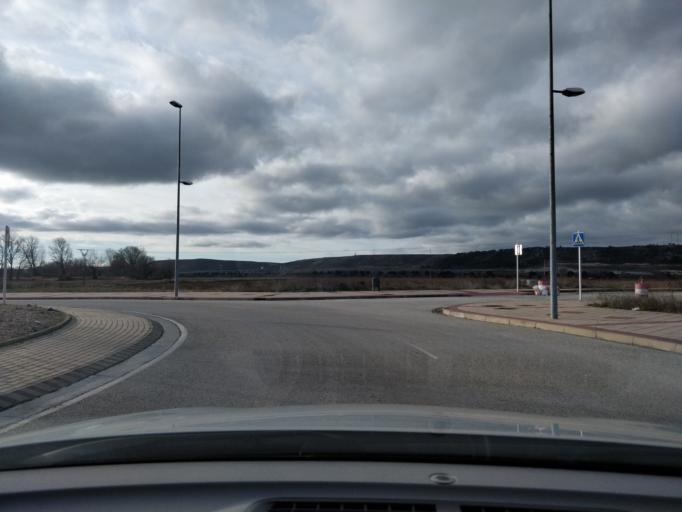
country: ES
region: Castille and Leon
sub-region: Provincia de Burgos
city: Villalbilla de Burgos
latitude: 42.3513
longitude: -3.7669
